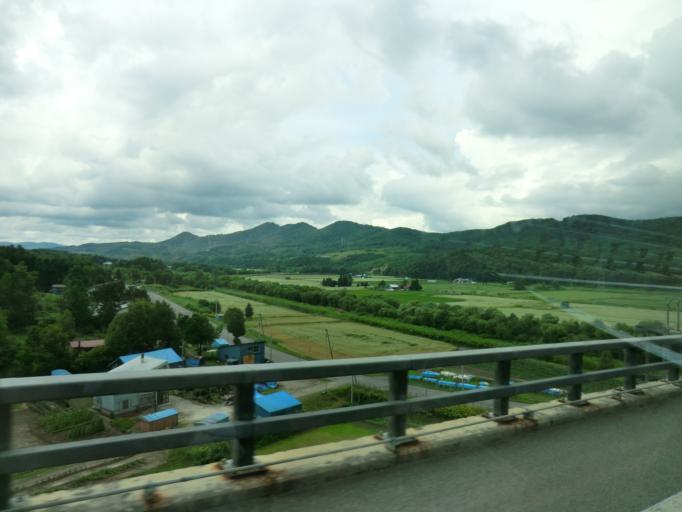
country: JP
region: Hokkaido
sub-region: Asahikawa-shi
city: Asahikawa
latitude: 43.7928
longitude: 142.2783
